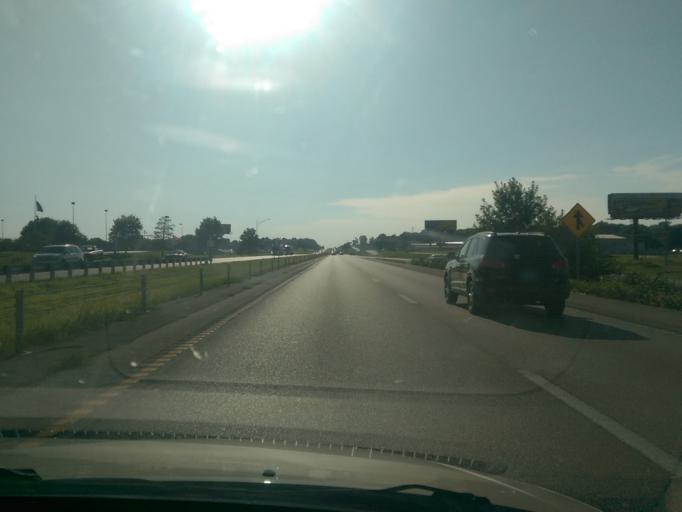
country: US
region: Missouri
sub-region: Jackson County
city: Grain Valley
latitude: 39.0216
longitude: -94.1991
